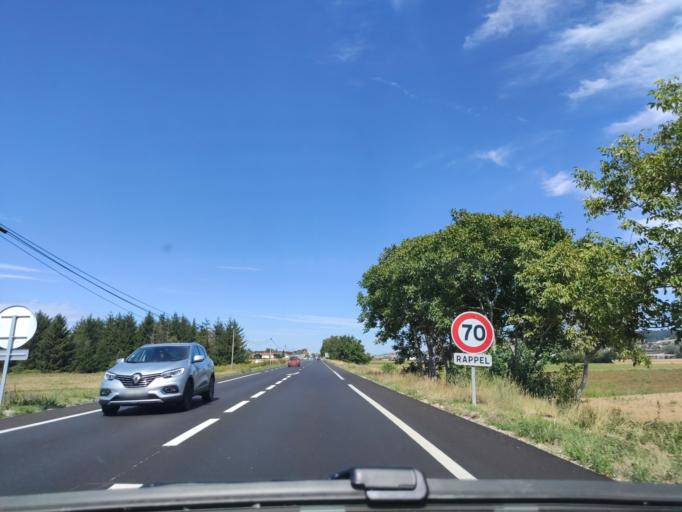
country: FR
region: Rhone-Alpes
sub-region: Departement de l'Isere
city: Reventin-Vaugris
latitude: 45.4533
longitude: 4.8239
